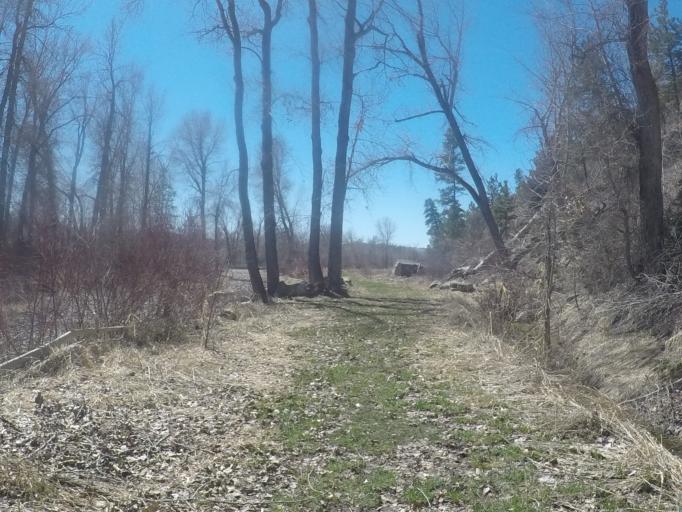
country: US
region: Montana
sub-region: Stillwater County
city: Columbus
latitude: 45.6199
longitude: -109.2912
